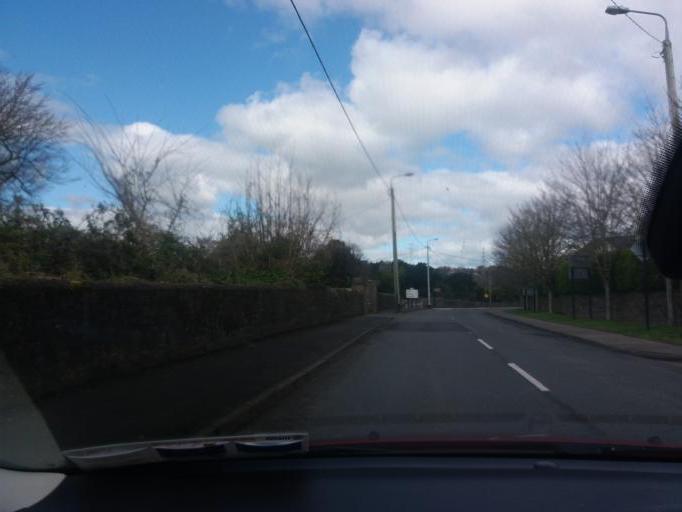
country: IE
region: Munster
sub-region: County Cork
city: Cobh
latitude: 51.8471
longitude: -8.3179
